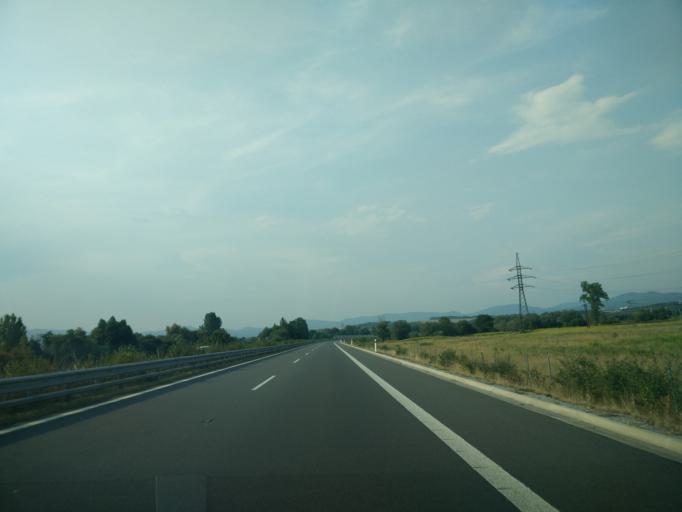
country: SK
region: Banskobystricky
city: Ziar nad Hronom
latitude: 48.5590
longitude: 18.8206
